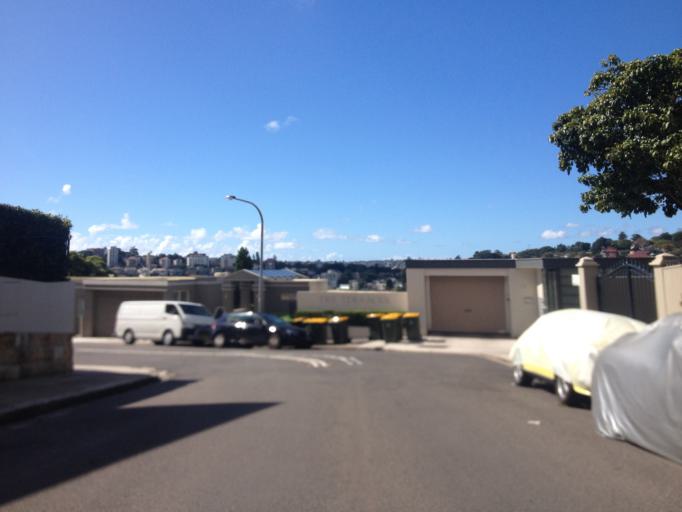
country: AU
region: New South Wales
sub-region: Woollahra
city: Darling Point
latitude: -33.8710
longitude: 151.2400
